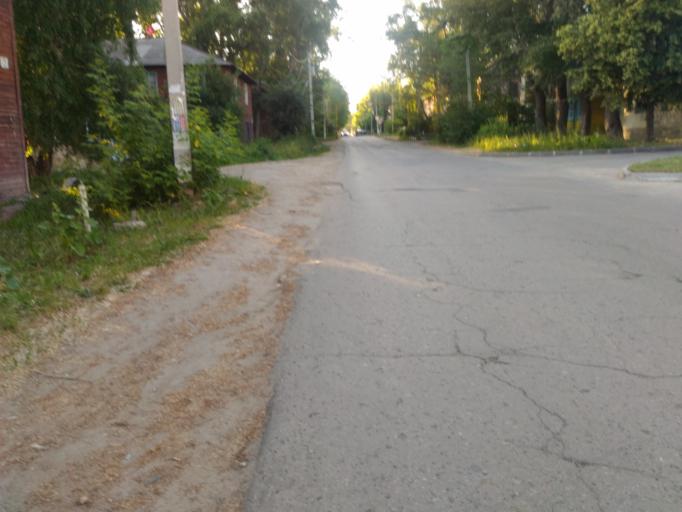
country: RU
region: Ulyanovsk
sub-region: Ulyanovskiy Rayon
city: Ulyanovsk
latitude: 54.3381
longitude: 48.3789
